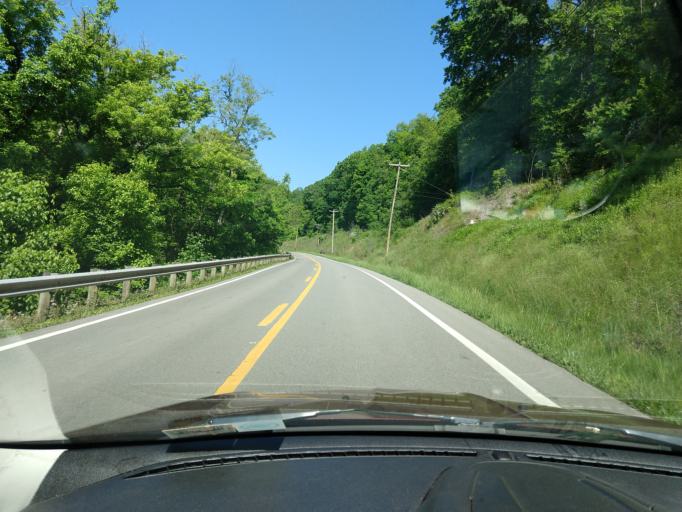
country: US
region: West Virginia
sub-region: Gilmer County
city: Glenville
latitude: 38.8793
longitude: -80.7127
